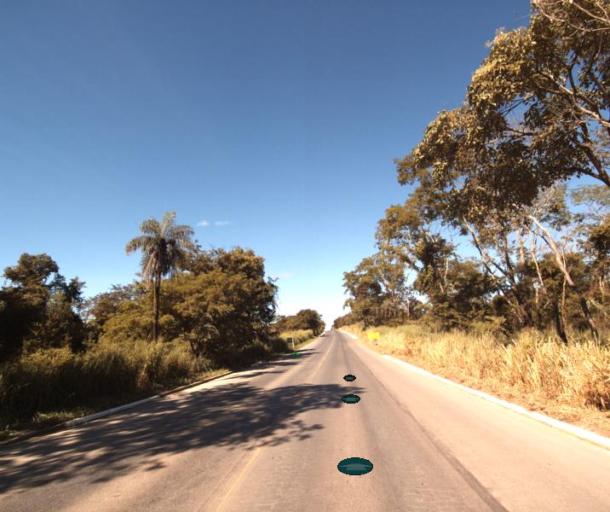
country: BR
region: Goias
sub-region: Itapaci
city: Itapaci
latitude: -14.9859
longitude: -49.4014
